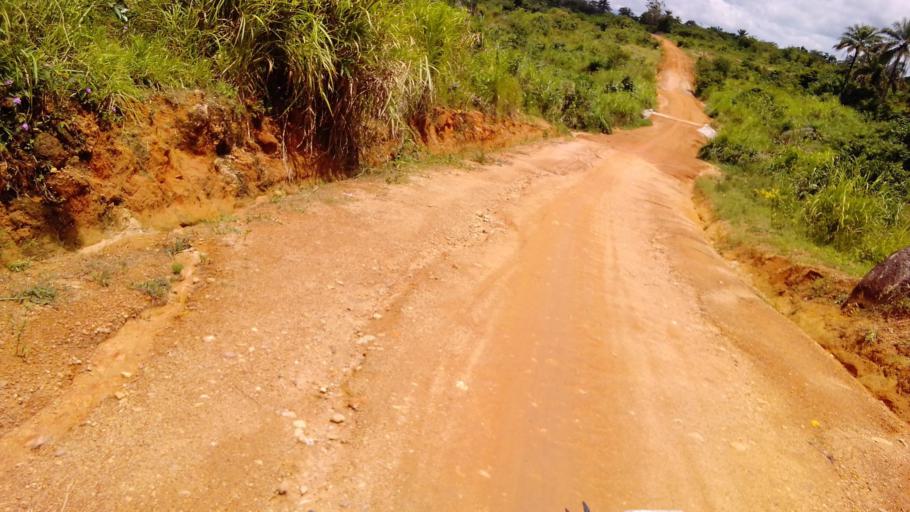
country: SL
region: Eastern Province
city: Koidu
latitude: 8.6909
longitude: -10.9256
